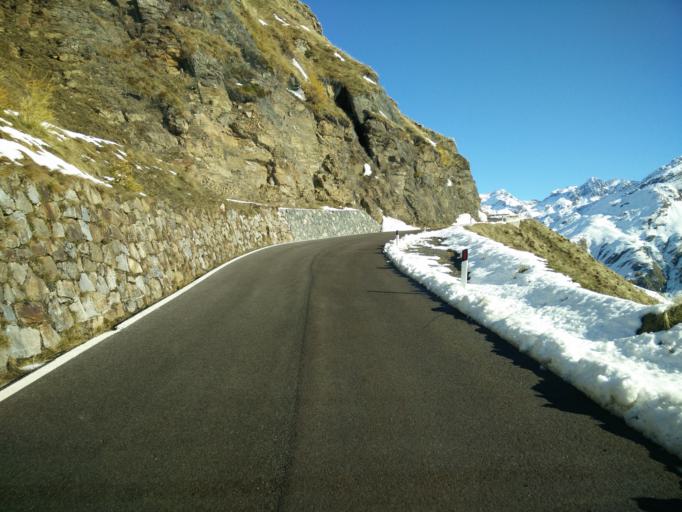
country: IT
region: Trentino-Alto Adige
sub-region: Bolzano
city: Moso in Passiria
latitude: 46.8879
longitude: 11.1182
